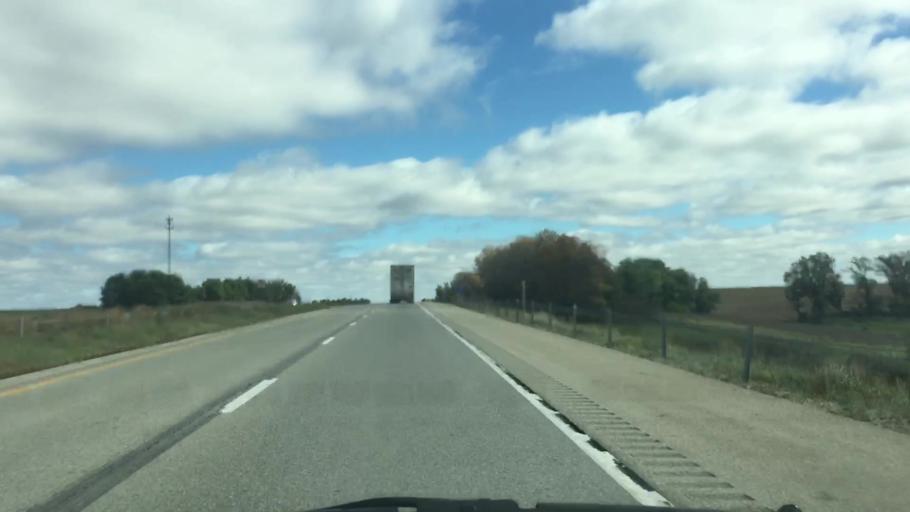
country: US
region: Iowa
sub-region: Poweshiek County
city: Grinnell
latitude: 41.6951
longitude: -92.8124
